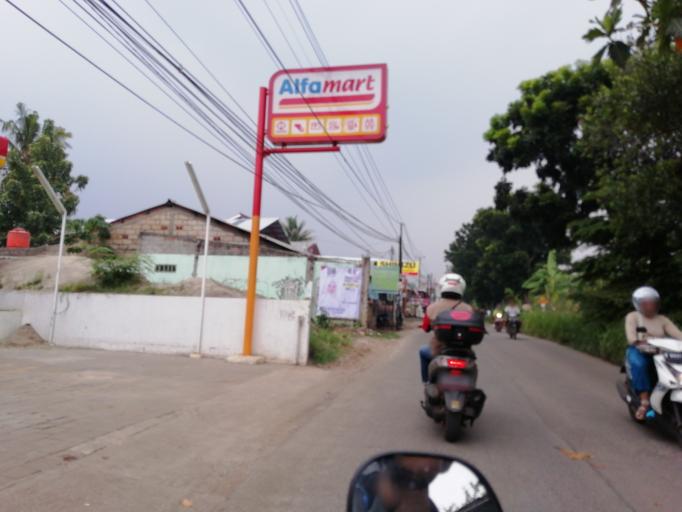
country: ID
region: West Java
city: Cibinong
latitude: -6.4747
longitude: 106.8033
